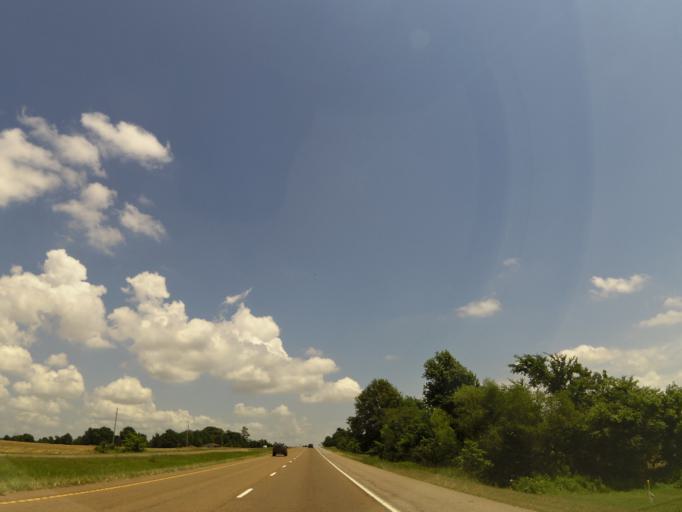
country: US
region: Tennessee
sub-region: Lauderdale County
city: Halls
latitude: 35.9412
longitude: -89.2994
